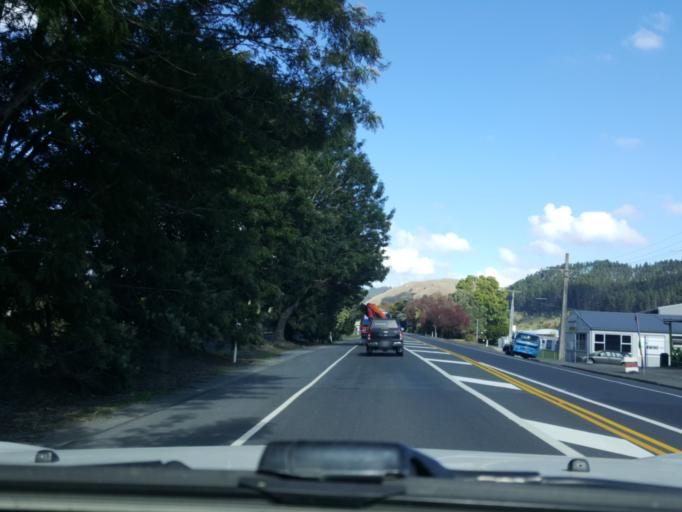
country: NZ
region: Waikato
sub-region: Waikato District
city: Ngaruawahia
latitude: -37.5789
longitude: 175.1596
